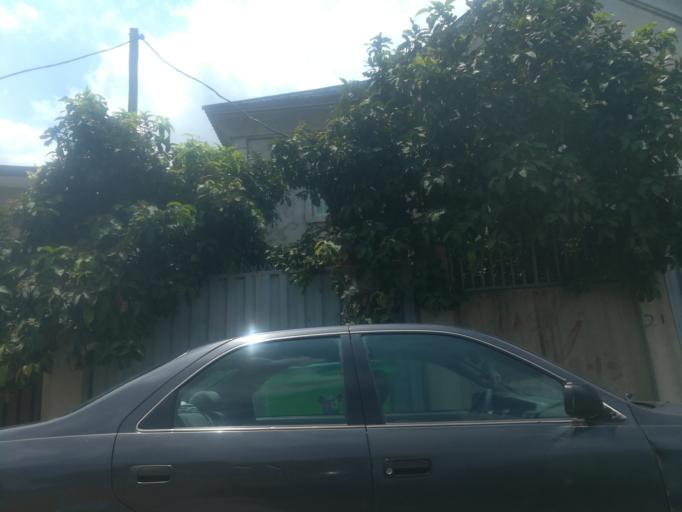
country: NG
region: Lagos
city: Ojota
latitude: 6.5624
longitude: 3.3944
